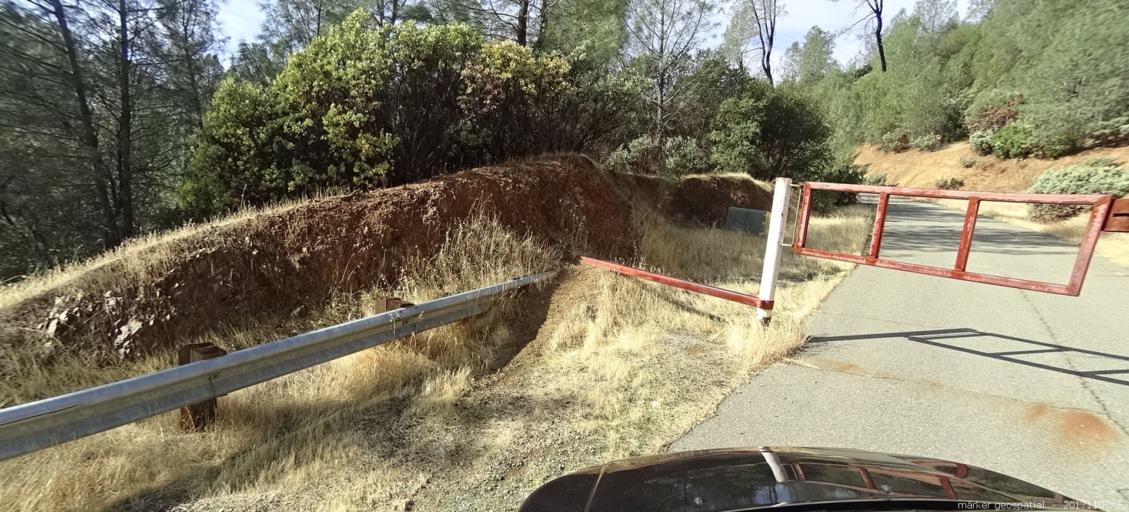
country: US
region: California
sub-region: Shasta County
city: Shasta
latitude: 40.5694
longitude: -122.4485
